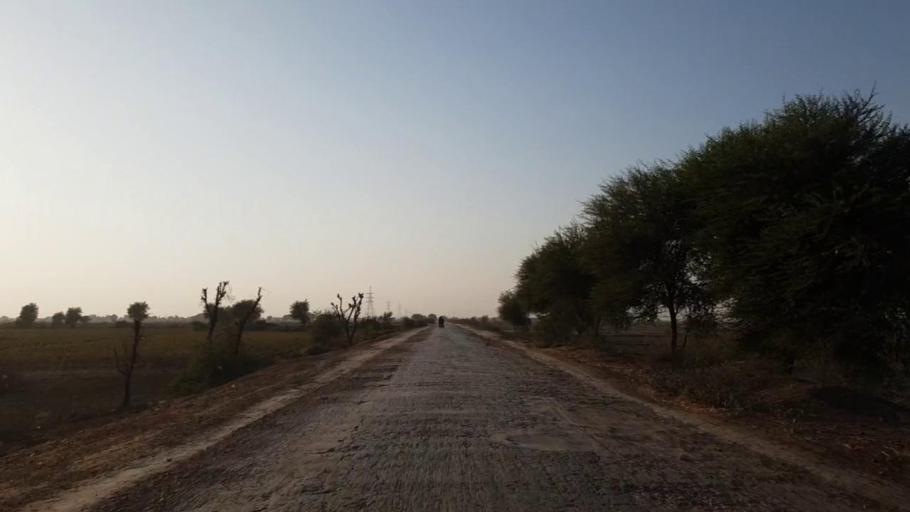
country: PK
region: Sindh
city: Chambar
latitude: 25.2137
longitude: 68.7730
